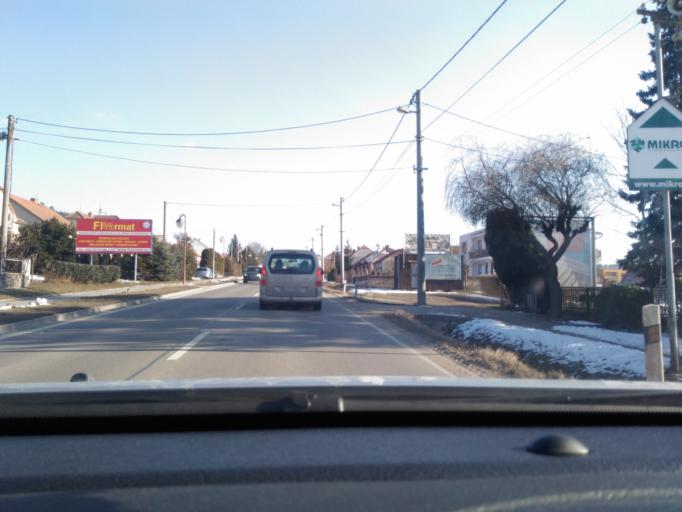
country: CZ
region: South Moravian
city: Cebin
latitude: 49.3184
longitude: 16.4705
